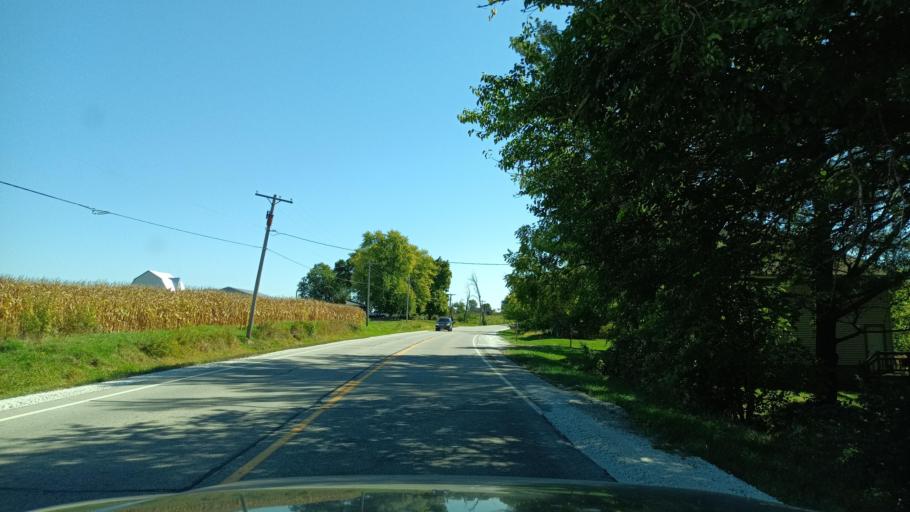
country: US
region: Illinois
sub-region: Peoria County
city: Hanna City
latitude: 40.7945
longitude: -89.7782
